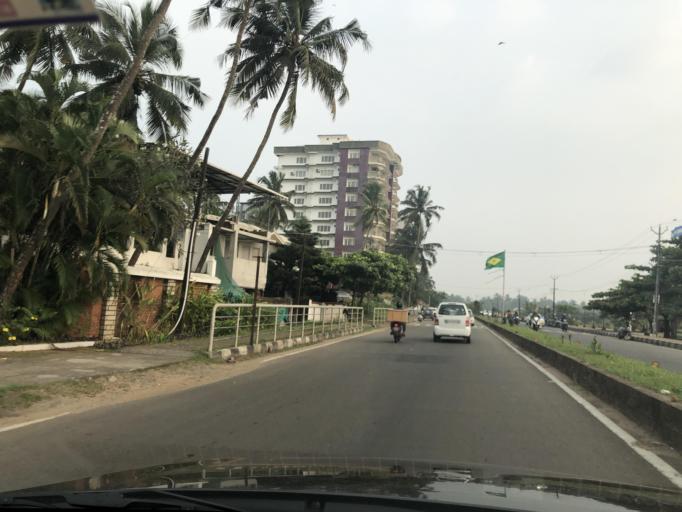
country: IN
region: Kerala
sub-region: Kozhikode
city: Kozhikode
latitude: 11.2782
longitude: 75.7629
